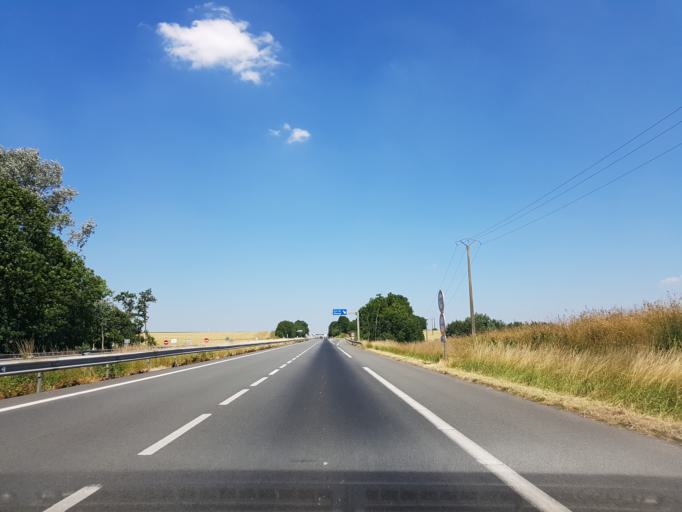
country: FR
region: Nord-Pas-de-Calais
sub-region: Departement du Nord
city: Marcoing
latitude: 50.0854
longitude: 3.1725
